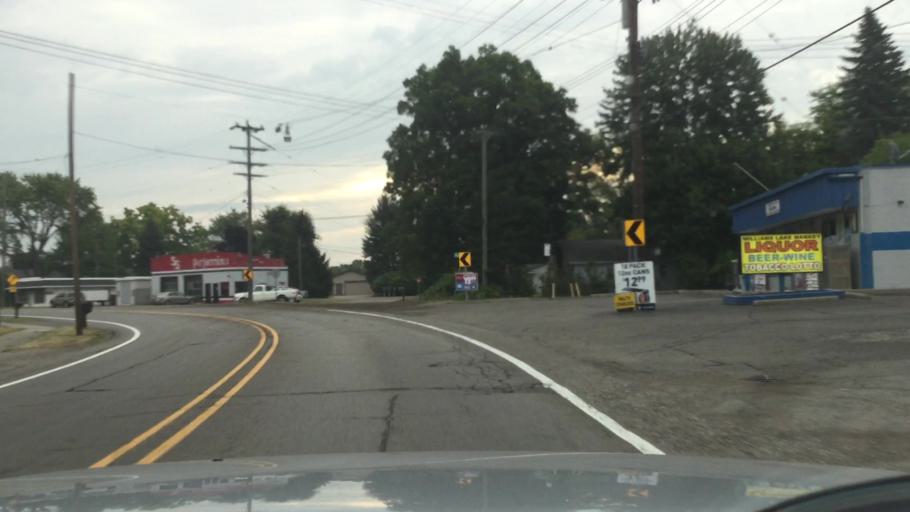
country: US
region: Michigan
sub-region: Oakland County
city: Waterford
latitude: 42.6813
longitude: -83.4254
